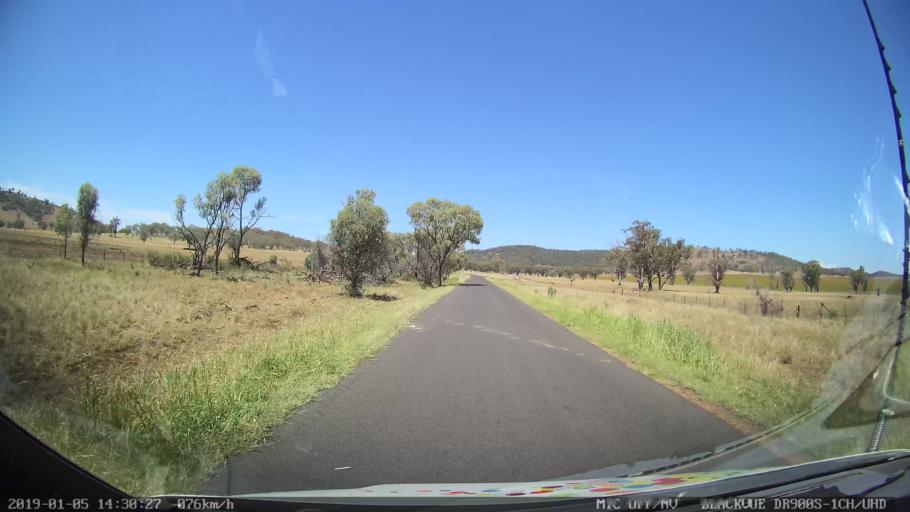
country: AU
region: New South Wales
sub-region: Tamworth Municipality
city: Phillip
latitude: -31.2279
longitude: 150.5930
